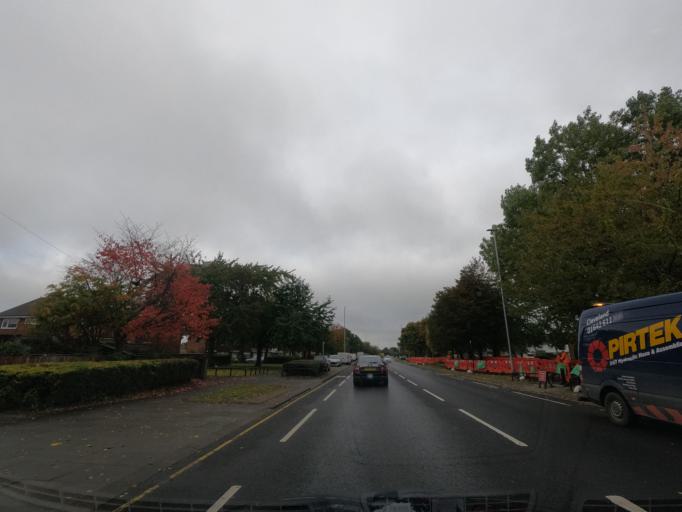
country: GB
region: England
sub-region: Middlesbrough
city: Nunthorpe
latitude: 54.5539
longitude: -1.1835
